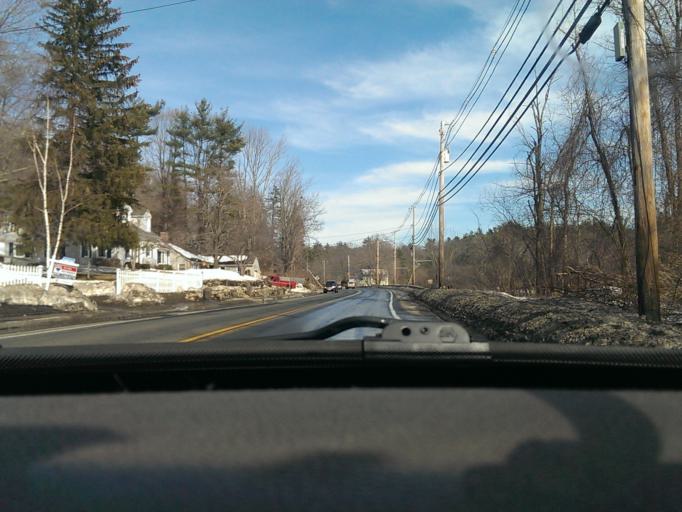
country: US
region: Massachusetts
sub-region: Hampden County
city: Palmer
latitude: 42.1801
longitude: -72.3178
